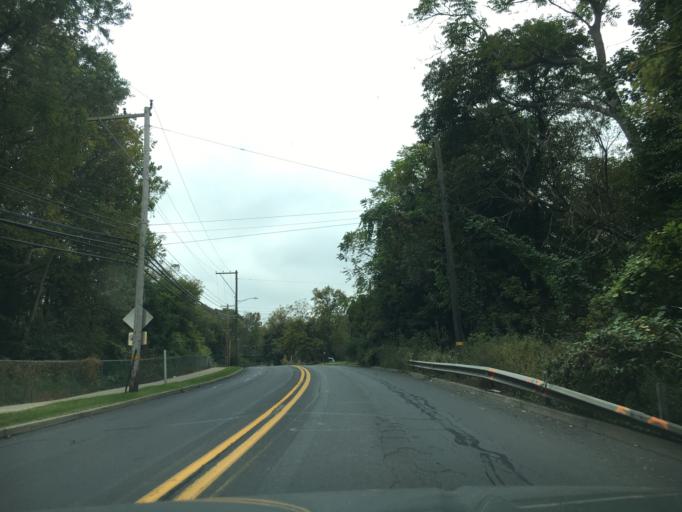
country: US
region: Pennsylvania
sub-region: Lehigh County
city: Cementon
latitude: 40.6876
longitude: -75.5134
